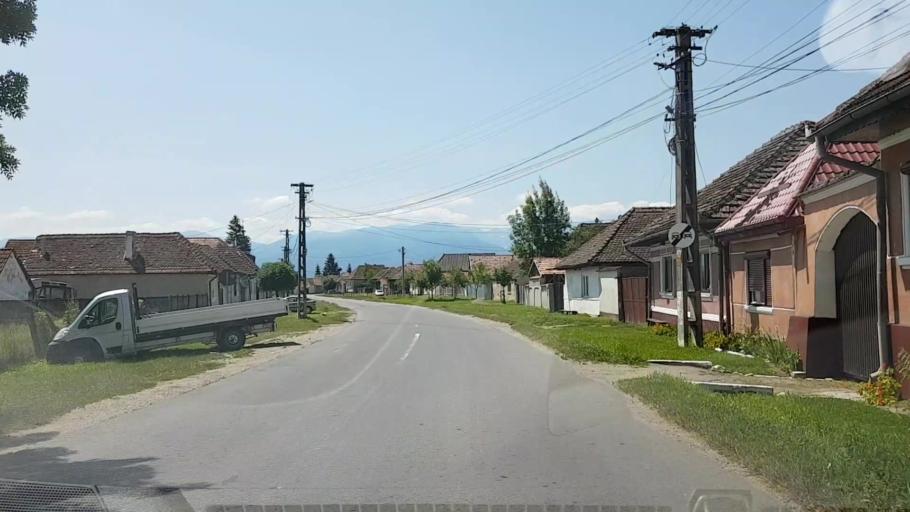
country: RO
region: Brasov
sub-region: Comuna Voila
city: Voila
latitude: 45.8427
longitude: 24.8327
